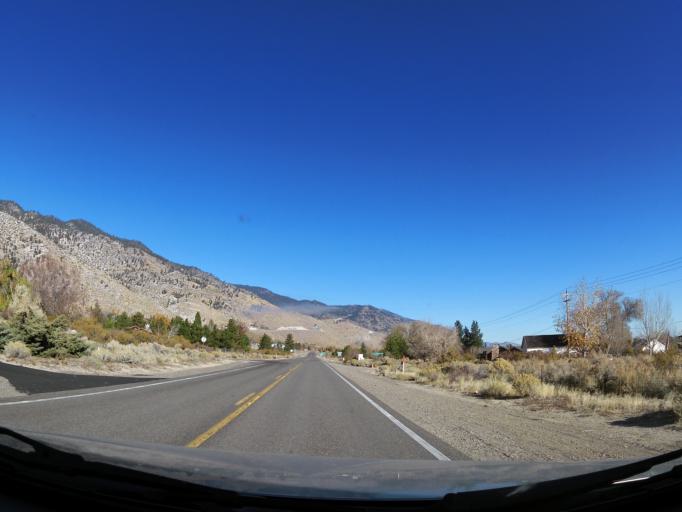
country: US
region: Nevada
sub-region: Douglas County
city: Minden
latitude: 38.9243
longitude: -119.8372
